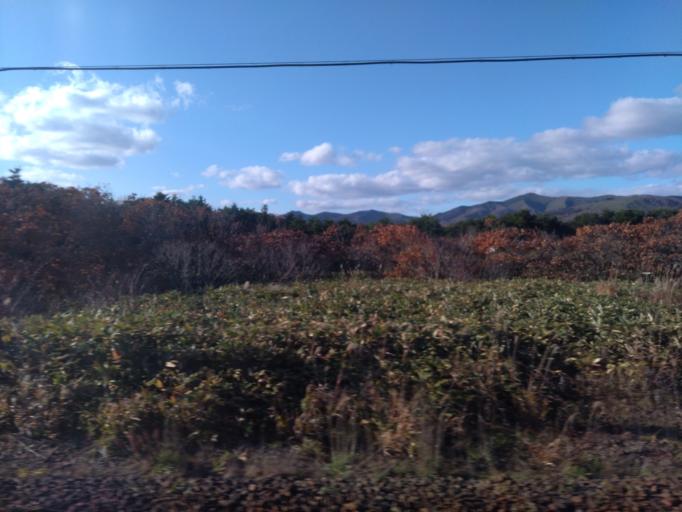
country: JP
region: Hokkaido
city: Niseko Town
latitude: 42.5491
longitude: 140.4160
